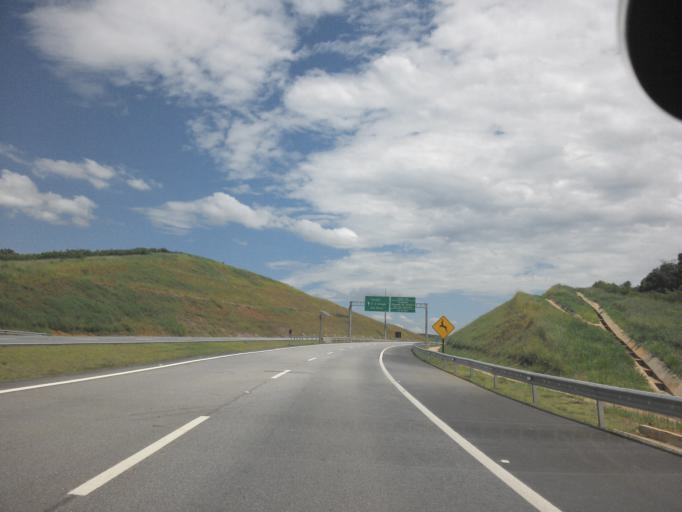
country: BR
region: Sao Paulo
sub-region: Taubate
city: Taubate
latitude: -23.1010
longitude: -45.5907
